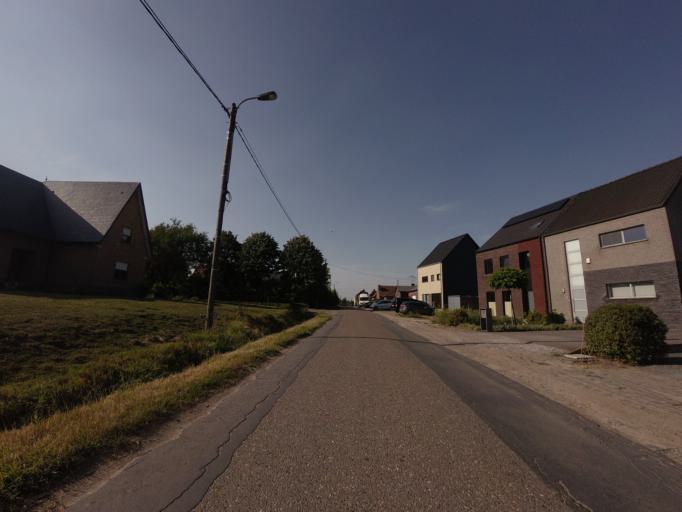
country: BE
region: Flanders
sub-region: Provincie Antwerpen
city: Kontich
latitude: 51.0975
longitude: 4.4617
